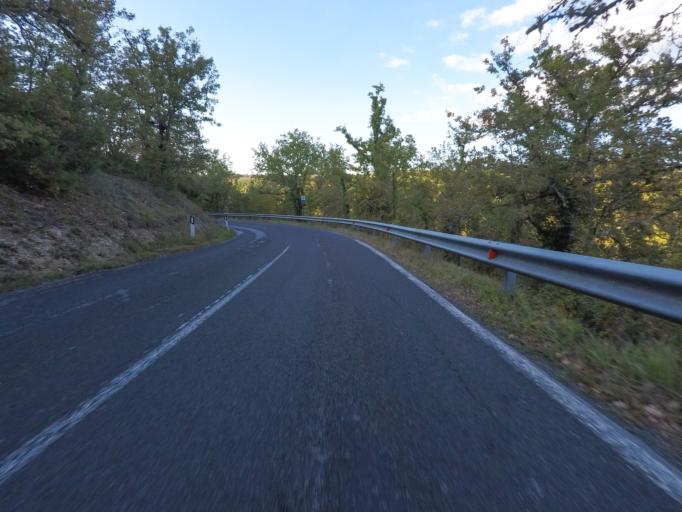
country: IT
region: Tuscany
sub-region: Provincia di Siena
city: Radda in Chianti
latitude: 43.4625
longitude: 11.3849
